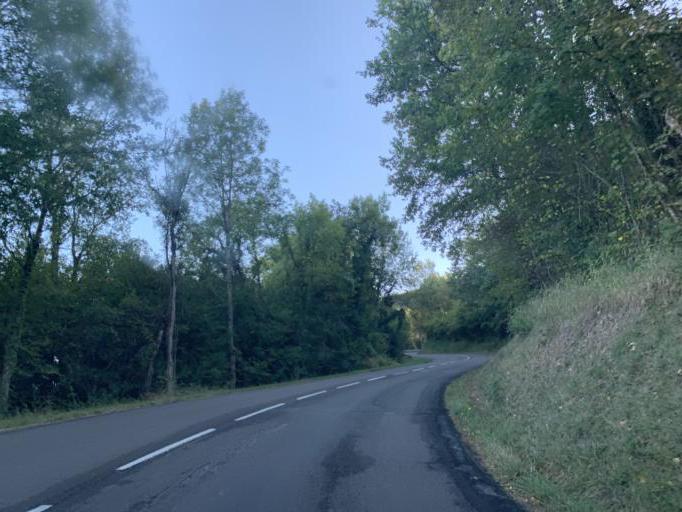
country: FR
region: Rhone-Alpes
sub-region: Departement de l'Ain
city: Belley
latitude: 45.7048
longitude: 5.6554
